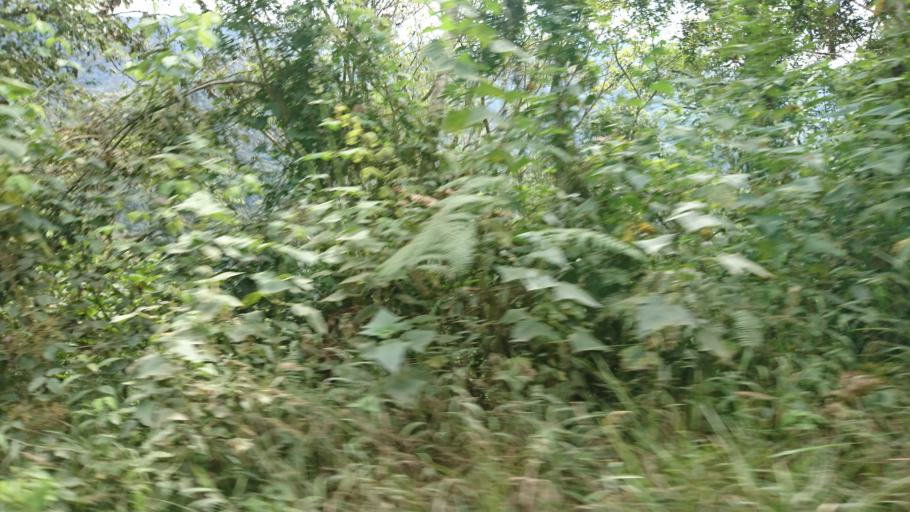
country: BO
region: La Paz
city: Coroico
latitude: -16.1100
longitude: -67.7791
